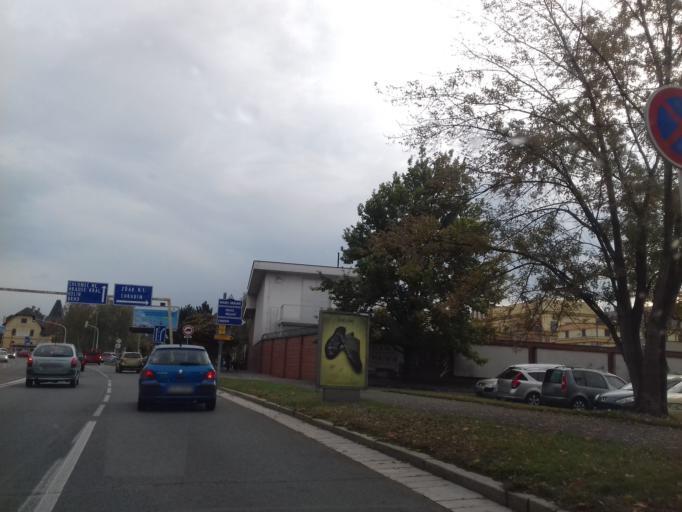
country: CZ
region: Pardubicky
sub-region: Okres Pardubice
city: Pardubice
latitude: 50.0338
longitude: 15.7795
